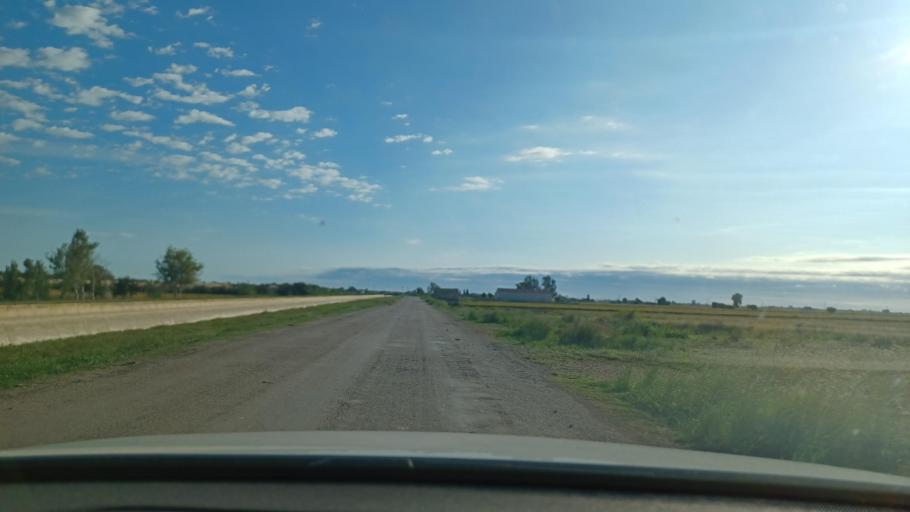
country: ES
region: Catalonia
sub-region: Provincia de Tarragona
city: Amposta
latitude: 40.7026
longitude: 0.6263
